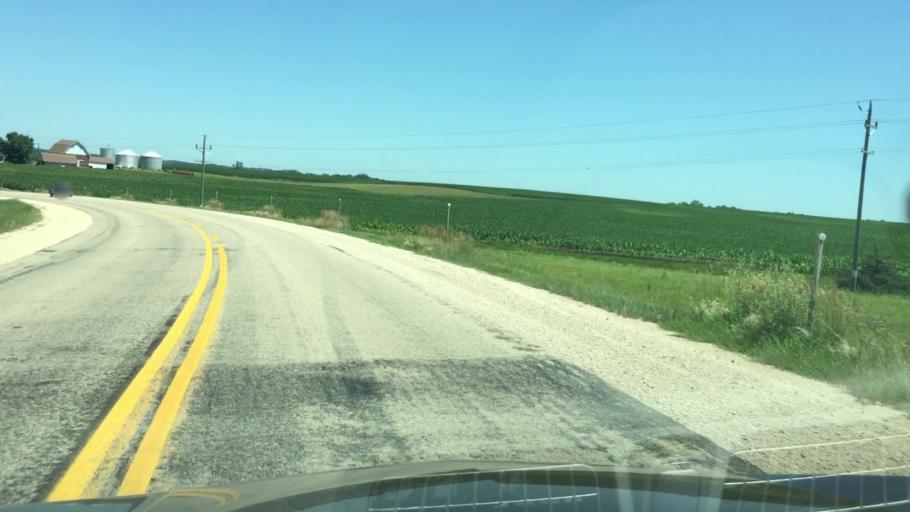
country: US
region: Iowa
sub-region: Cedar County
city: Mechanicsville
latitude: 41.9626
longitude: -91.1426
